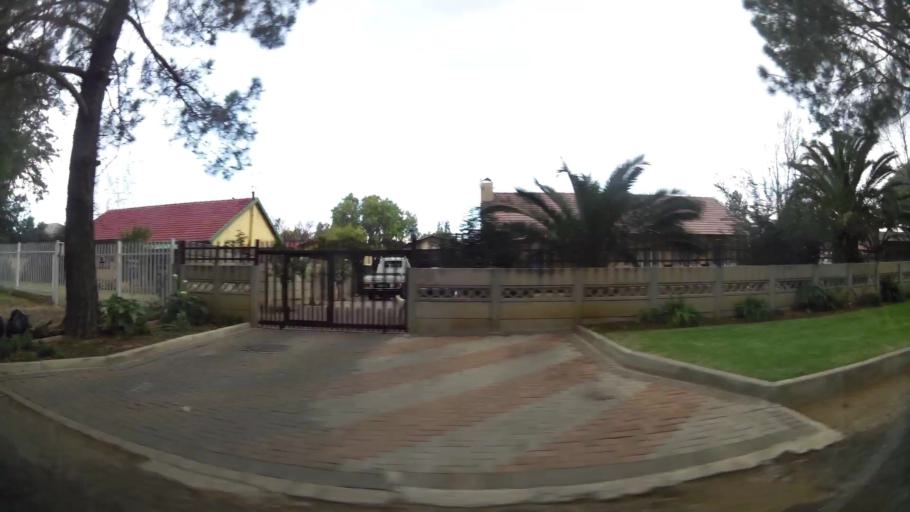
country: ZA
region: Orange Free State
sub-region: Lejweleputswa District Municipality
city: Welkom
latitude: -27.9666
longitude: 26.7248
